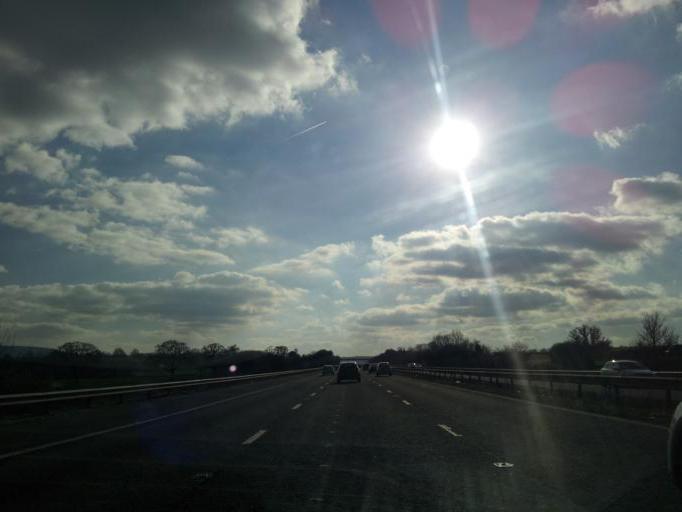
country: GB
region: England
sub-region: Somerset
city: Taunton
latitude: 50.9901
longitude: -3.0992
